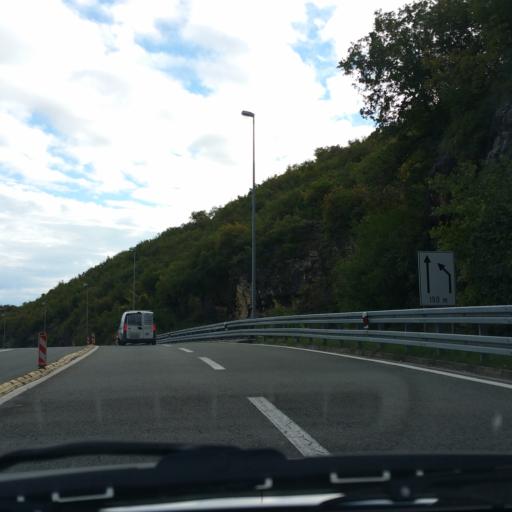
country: HR
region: Primorsko-Goranska
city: Drenova
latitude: 45.3457
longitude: 14.4203
